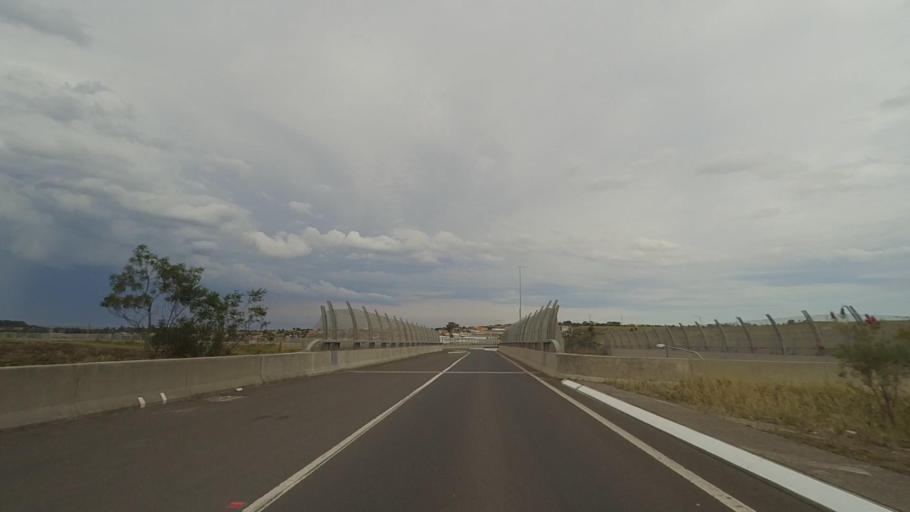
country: AU
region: New South Wales
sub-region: Shellharbour
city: Croom
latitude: -34.5887
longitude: 150.8438
